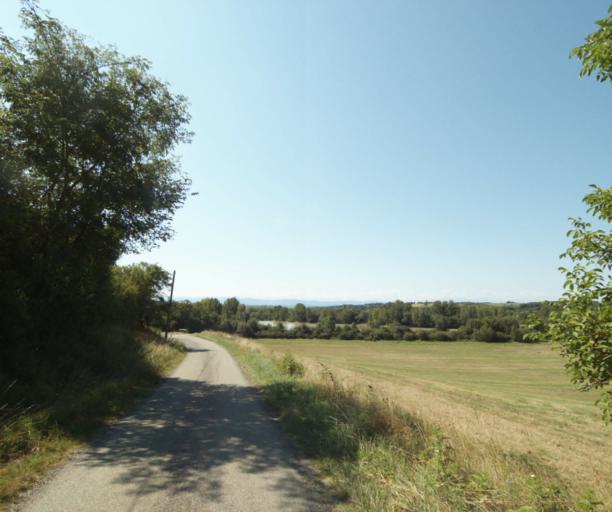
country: FR
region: Midi-Pyrenees
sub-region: Departement de l'Ariege
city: Lezat-sur-Leze
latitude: 43.2408
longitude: 1.3783
